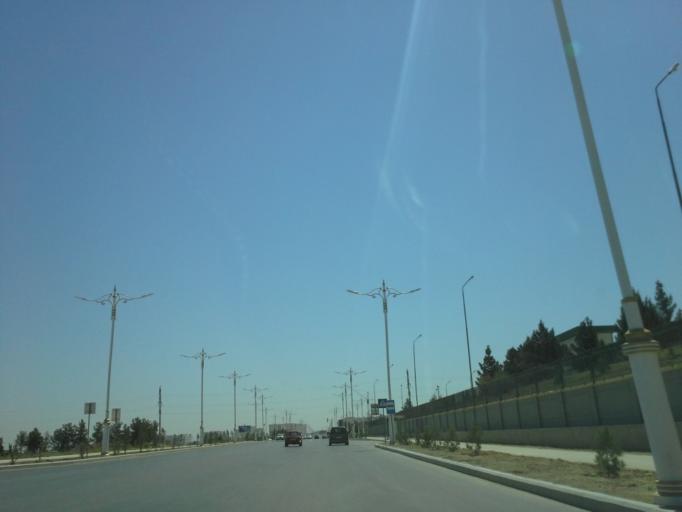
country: TM
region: Ahal
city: Ashgabat
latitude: 37.9005
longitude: 58.4024
